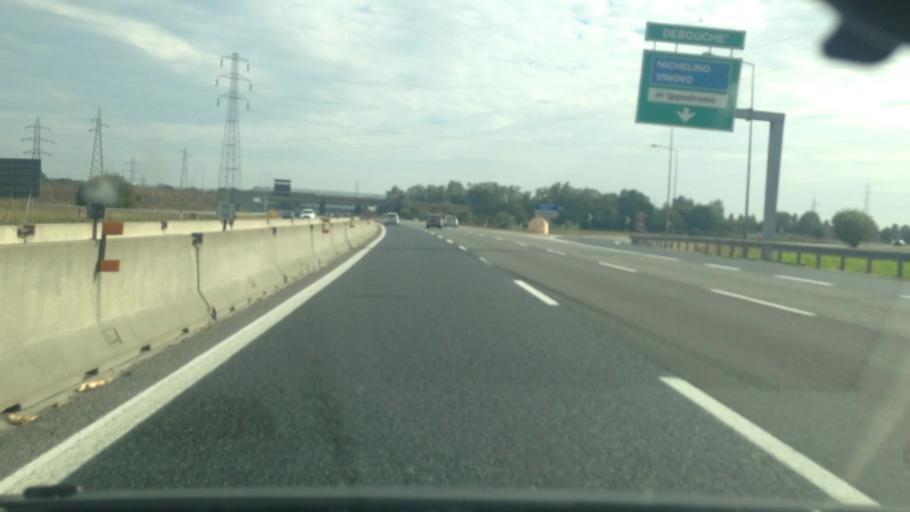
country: IT
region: Piedmont
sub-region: Provincia di Torino
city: Nichelino
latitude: 44.9964
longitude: 7.6256
